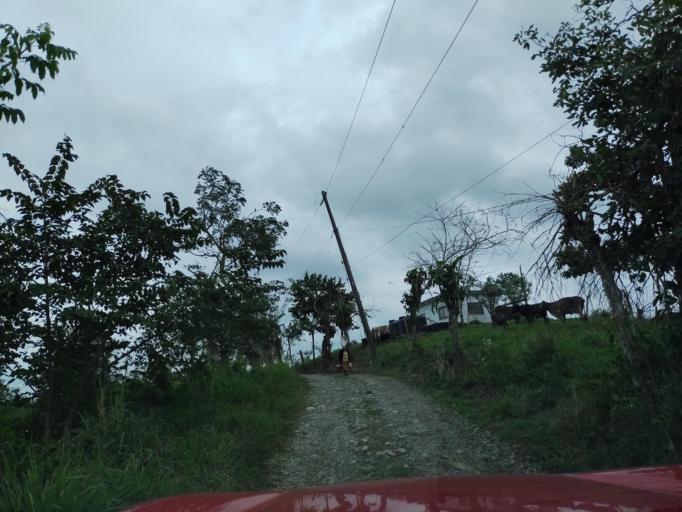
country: MX
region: Veracruz
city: Coatzintla
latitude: 20.4567
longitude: -97.4127
